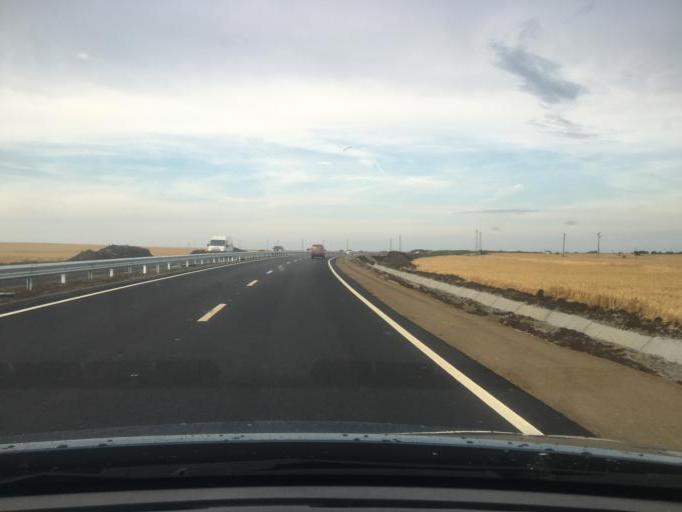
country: BG
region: Burgas
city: Aheloy
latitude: 42.6564
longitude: 27.6536
